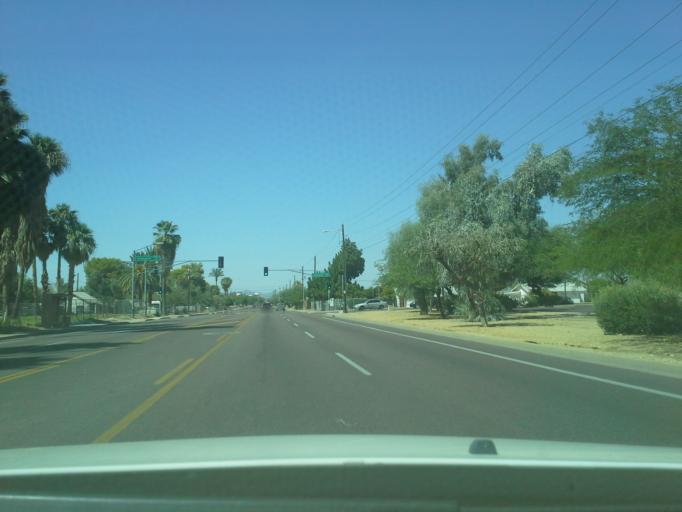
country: US
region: Arizona
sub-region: Maricopa County
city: Phoenix
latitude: 33.3841
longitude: -112.0646
